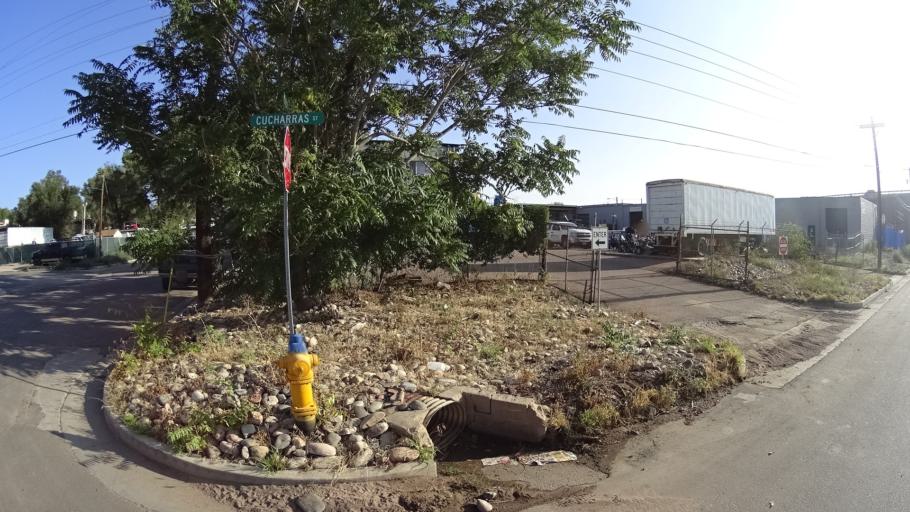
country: US
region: Colorado
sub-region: El Paso County
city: Colorado Springs
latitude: 38.8314
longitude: -104.8359
